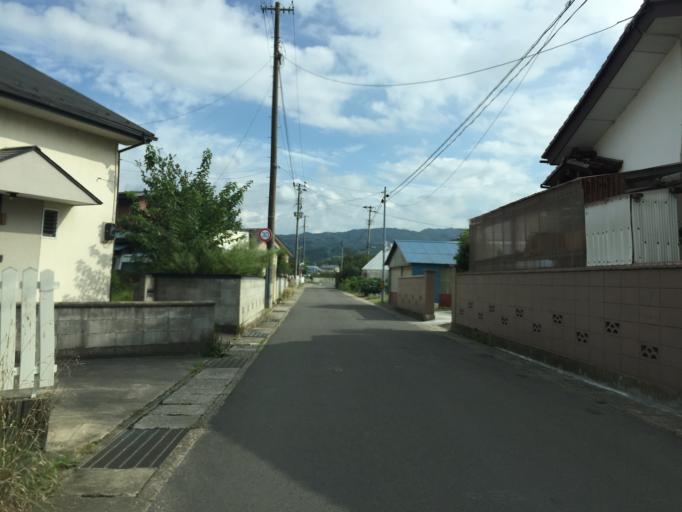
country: JP
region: Fukushima
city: Fukushima-shi
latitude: 37.7750
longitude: 140.5072
